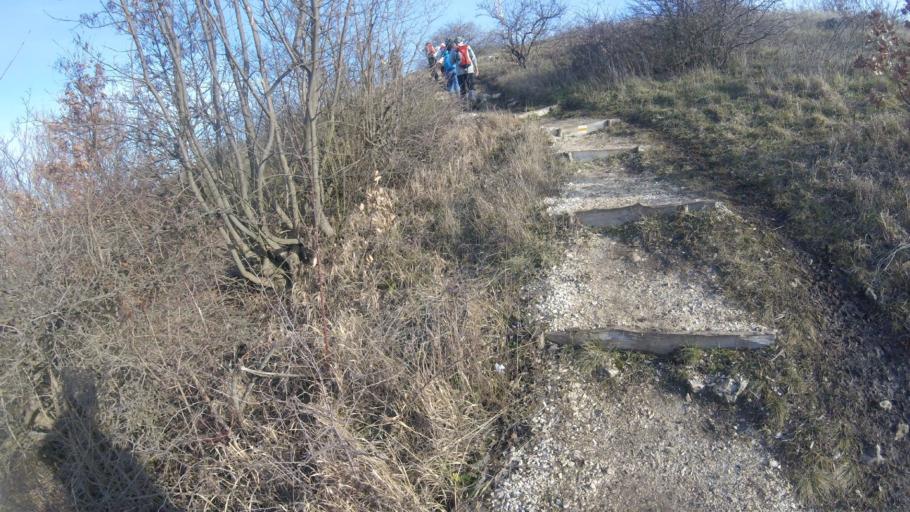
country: HU
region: Pest
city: Nagykovacsi
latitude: 47.6464
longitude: 19.0054
